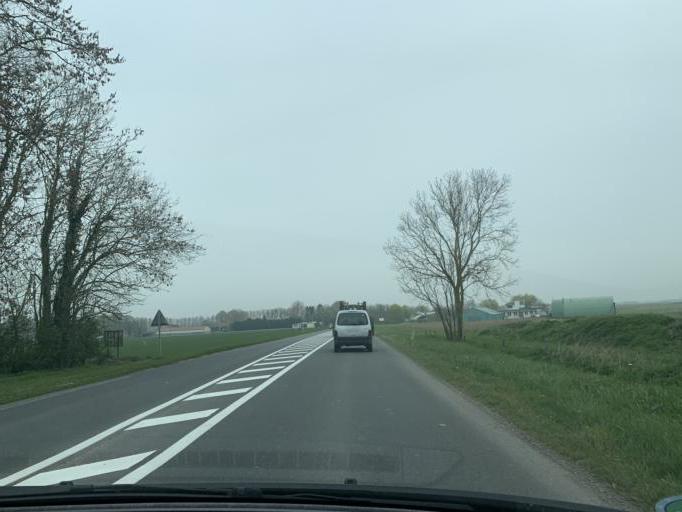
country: FR
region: Picardie
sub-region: Departement de la Somme
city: Abbeville
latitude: 50.1371
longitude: 1.8254
